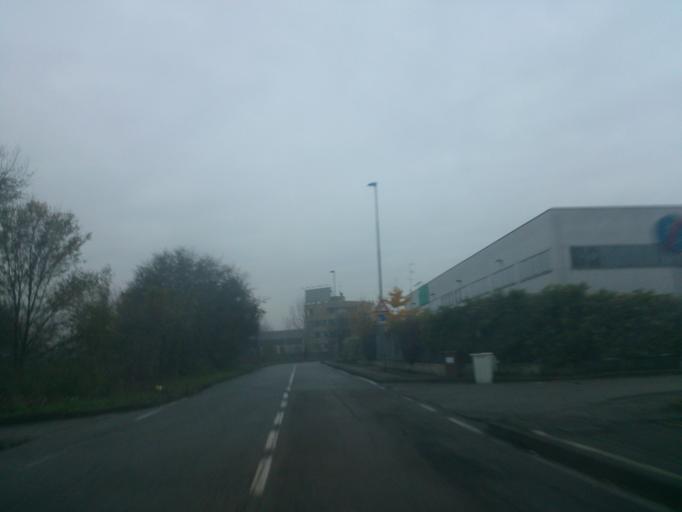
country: IT
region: Lombardy
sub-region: Citta metropolitana di Milano
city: San Donato Milanese
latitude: 45.4105
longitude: 9.2615
